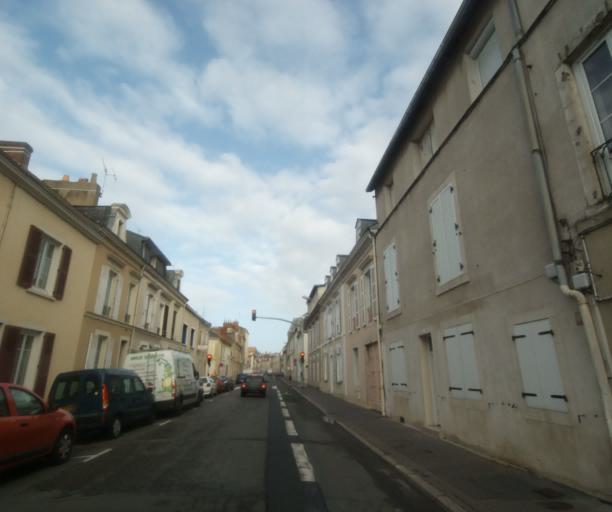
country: FR
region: Pays de la Loire
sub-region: Departement de la Sarthe
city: Le Mans
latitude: 47.9978
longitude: 0.2031
